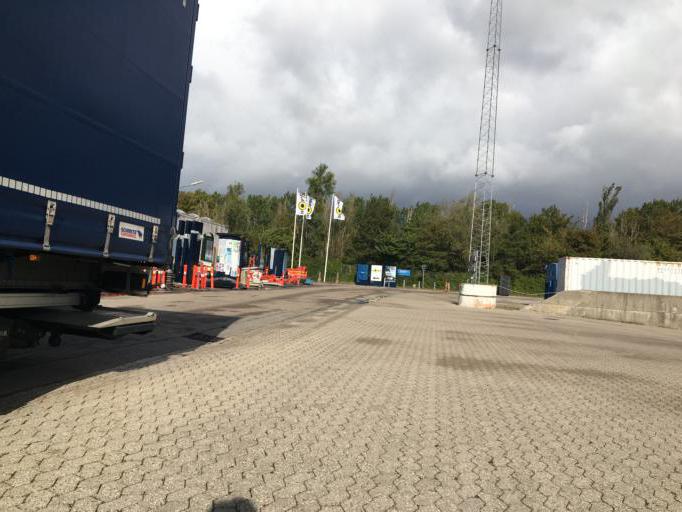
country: DK
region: Capital Region
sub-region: Hvidovre Kommune
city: Hvidovre
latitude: 55.6147
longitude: 12.4649
